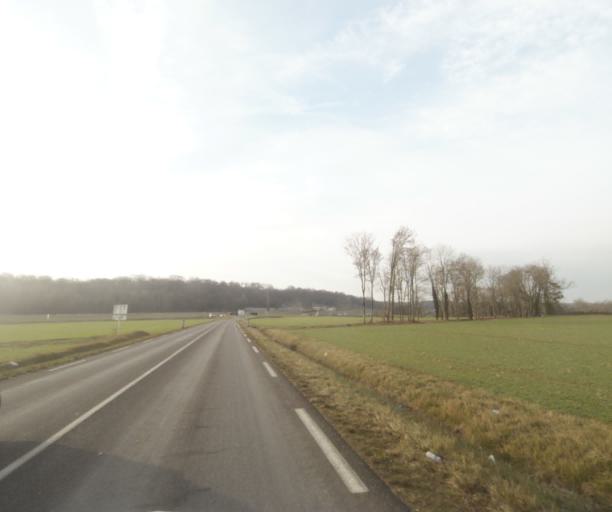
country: FR
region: Champagne-Ardenne
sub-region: Departement de la Haute-Marne
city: Saint-Dizier
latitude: 48.6226
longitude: 4.9291
